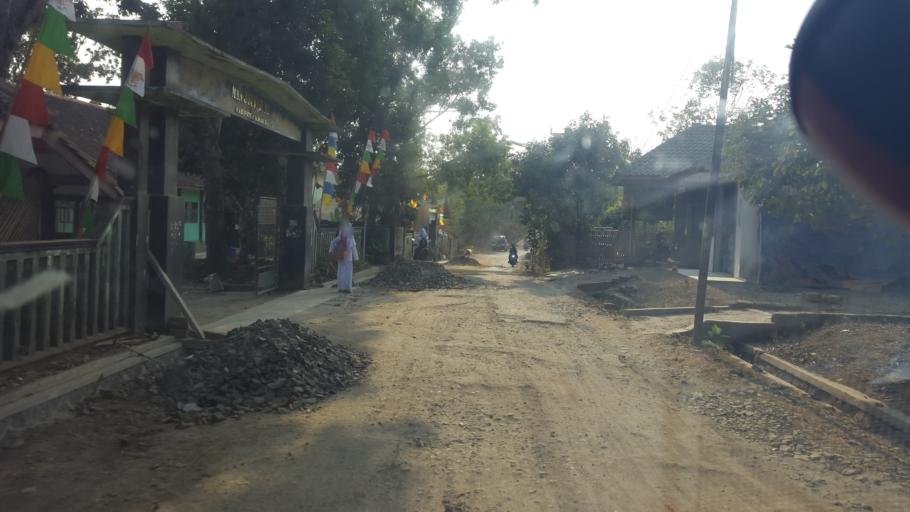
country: ID
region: West Java
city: Surade
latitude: -7.3381
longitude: 106.5595
